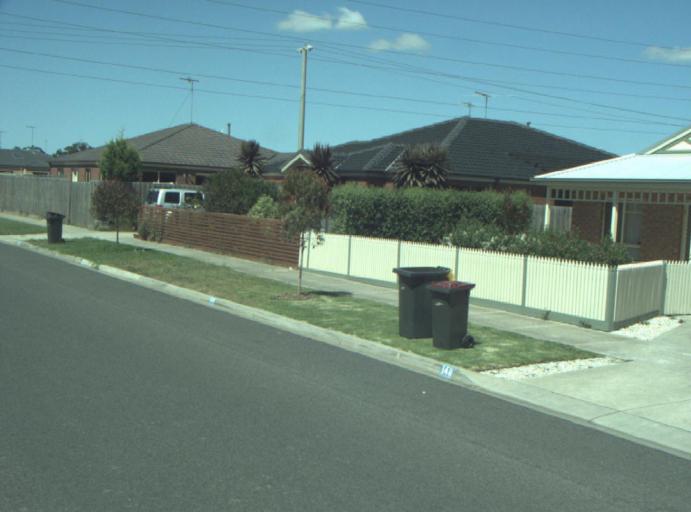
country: AU
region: Victoria
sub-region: Greater Geelong
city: Breakwater
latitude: -38.1982
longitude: 144.3475
